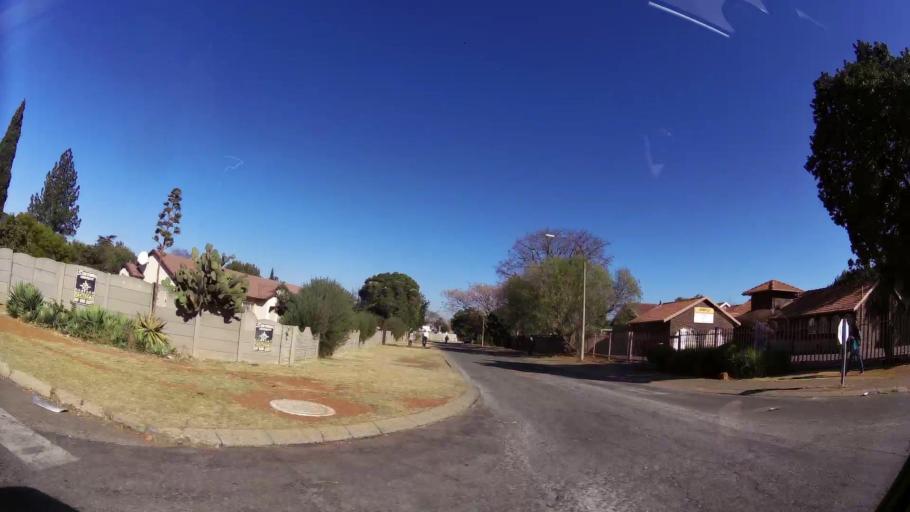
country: ZA
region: Gauteng
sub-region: Ekurhuleni Metropolitan Municipality
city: Germiston
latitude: -26.3277
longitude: 28.0982
